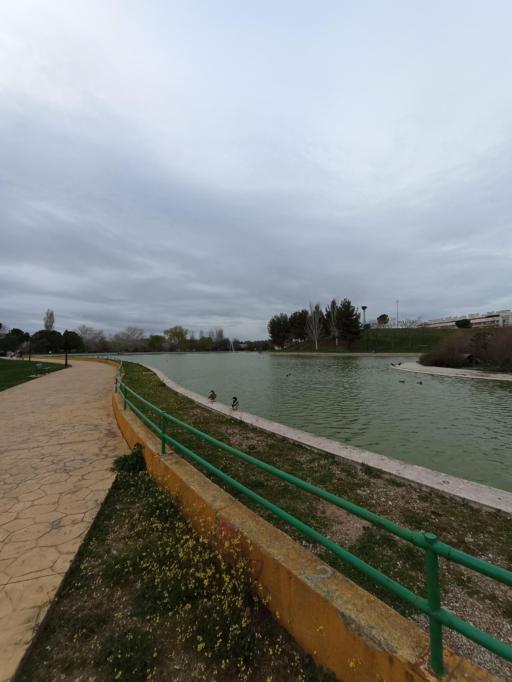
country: ES
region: Madrid
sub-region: Provincia de Madrid
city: Parla
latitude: 40.2162
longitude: -3.7604
